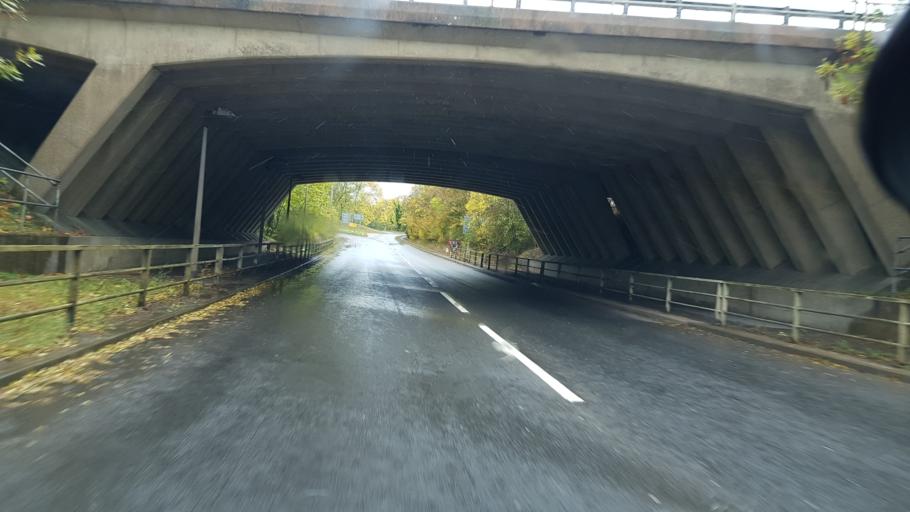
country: GB
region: England
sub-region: Gloucestershire
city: Tewkesbury
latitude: 52.0347
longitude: -2.1637
